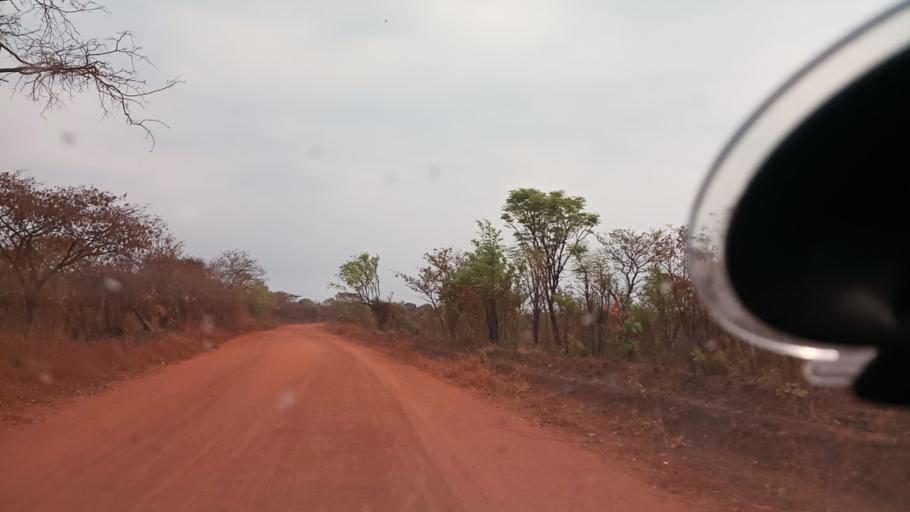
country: ZM
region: Luapula
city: Nchelenge
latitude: -9.1729
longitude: 28.2814
